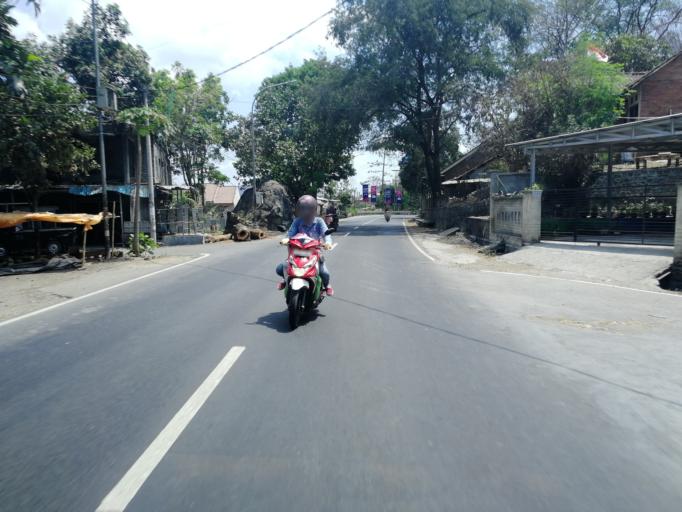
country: ID
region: West Nusa Tenggara
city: Jelateng Timur
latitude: -8.7092
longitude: 116.0778
